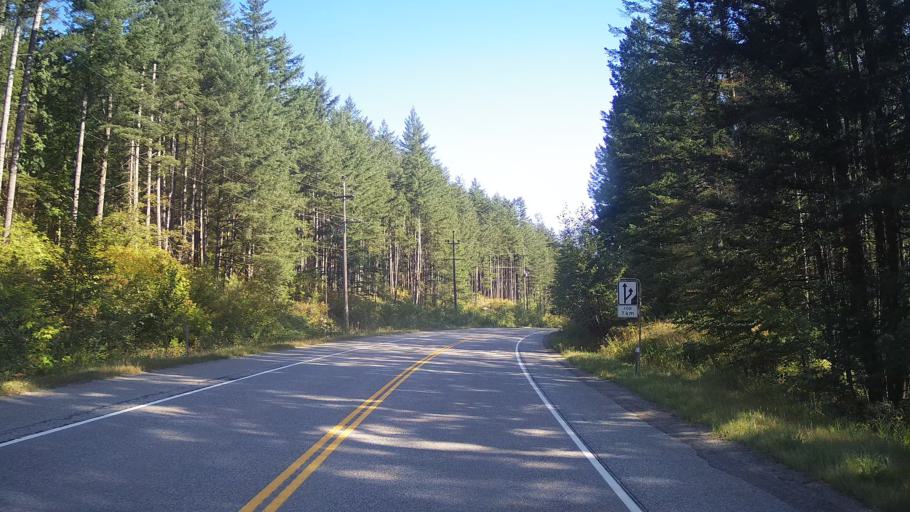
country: CA
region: British Columbia
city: Hope
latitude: 49.4336
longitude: -121.4394
